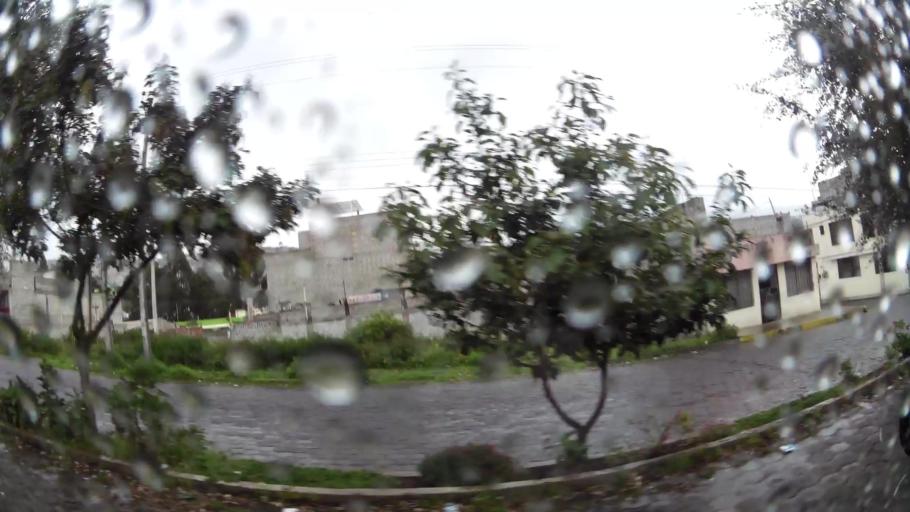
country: EC
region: Pichincha
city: Quito
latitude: -0.0973
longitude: -78.5003
